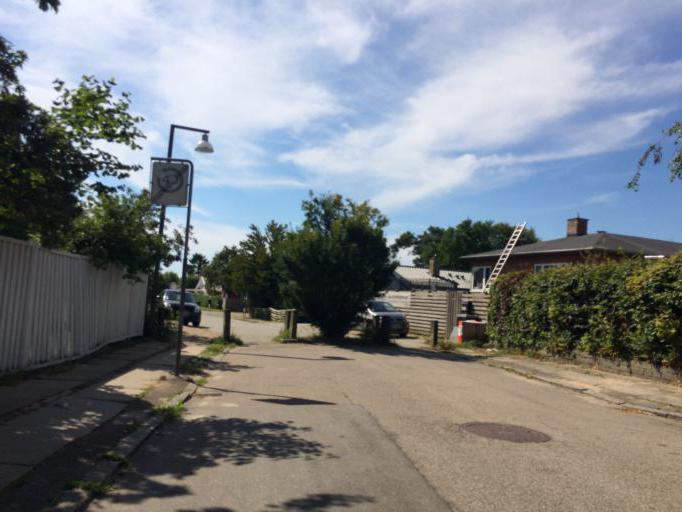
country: DK
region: Capital Region
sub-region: Herlev Kommune
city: Herlev
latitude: 55.7144
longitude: 12.4427
